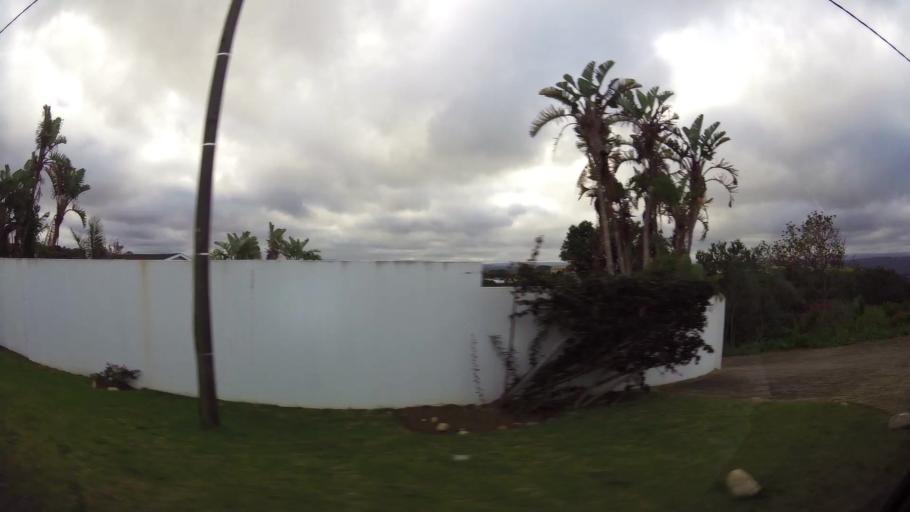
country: ZA
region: Western Cape
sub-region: Eden District Municipality
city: Plettenberg Bay
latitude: -34.0465
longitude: 23.3638
